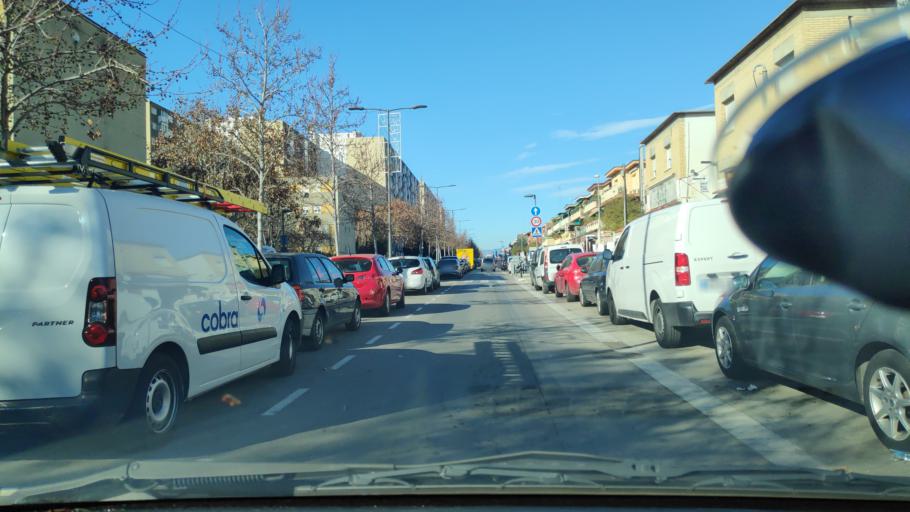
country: ES
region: Catalonia
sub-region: Provincia de Barcelona
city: Barbera del Valles
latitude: 41.5090
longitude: 2.1182
